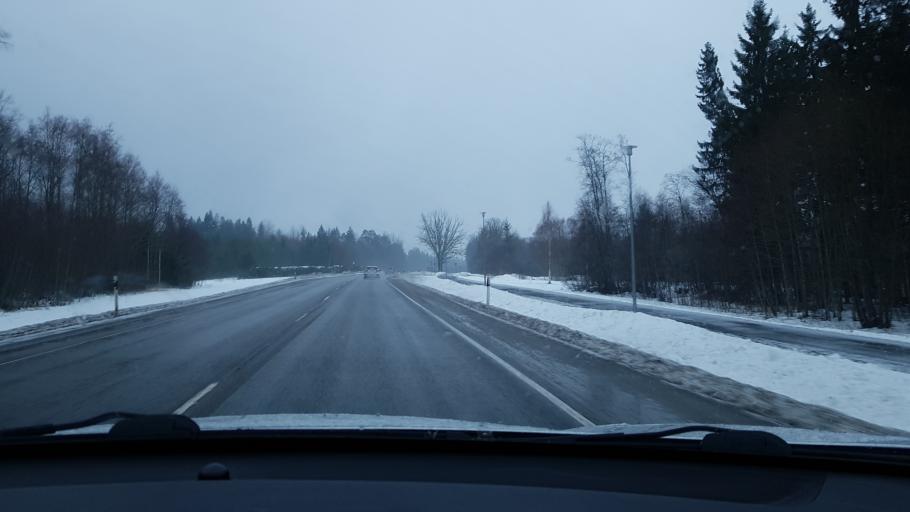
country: EE
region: Jaervamaa
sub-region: Paide linn
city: Paide
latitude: 58.8690
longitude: 25.4944
